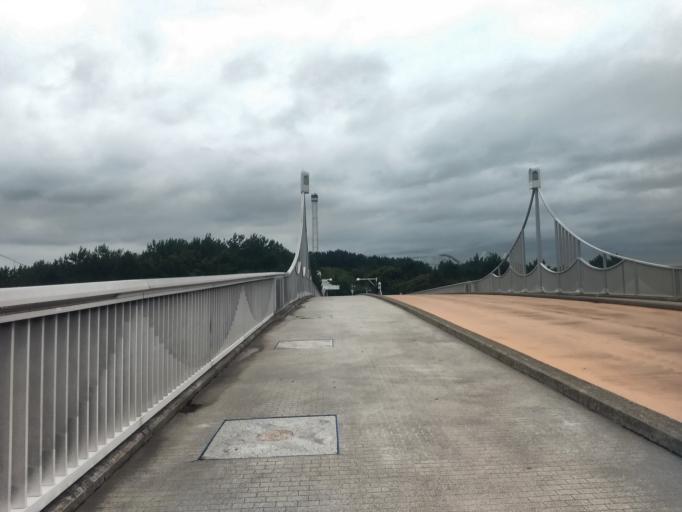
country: JP
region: Kanagawa
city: Yokosuka
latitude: 35.3389
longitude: 139.6421
